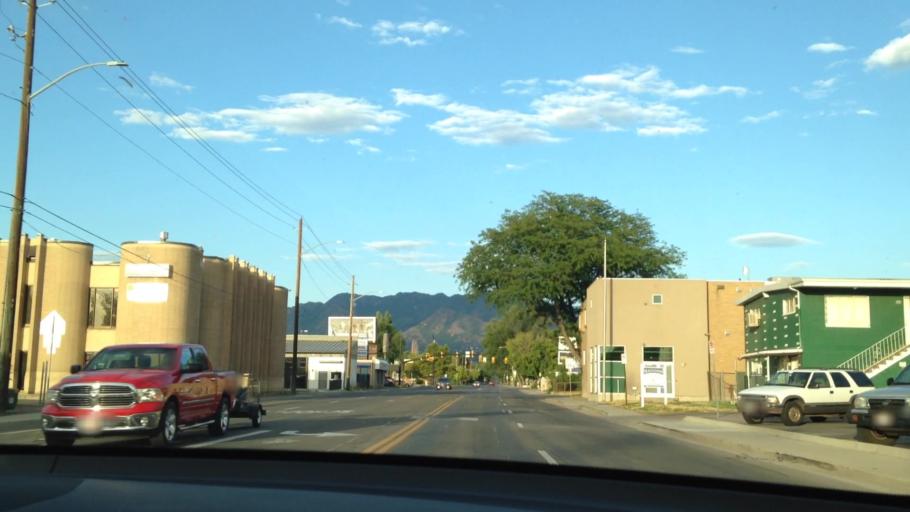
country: US
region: Utah
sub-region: Salt Lake County
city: South Salt Lake
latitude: 40.7335
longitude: -111.8908
